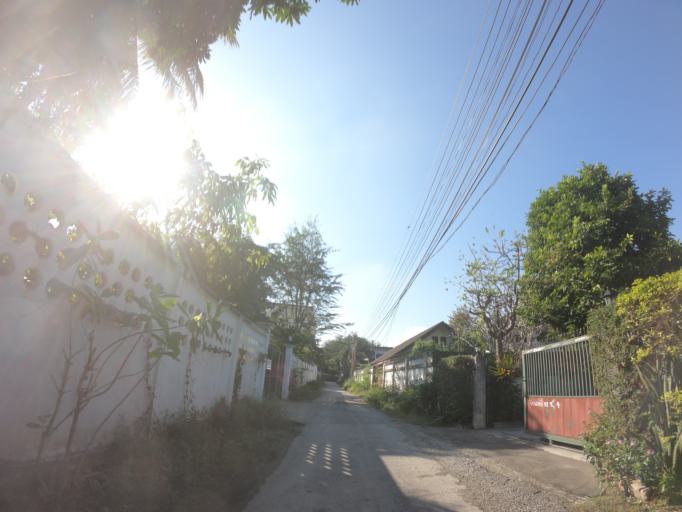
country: TH
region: Chiang Mai
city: Chiang Mai
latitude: 18.7870
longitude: 99.0232
